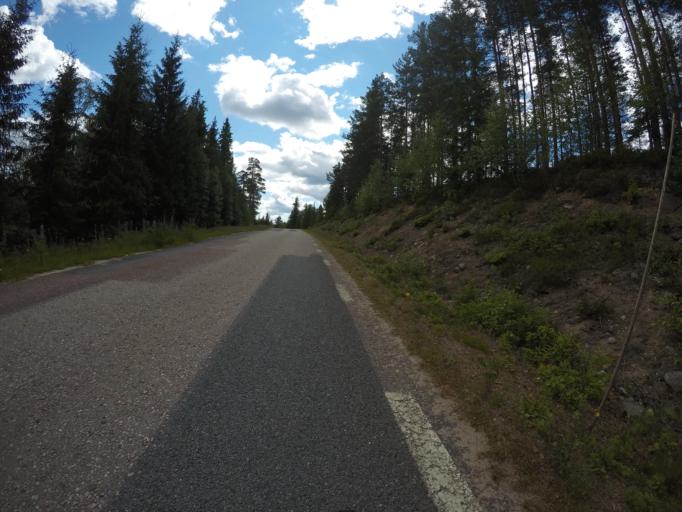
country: SE
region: OErebro
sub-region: Hallefors Kommun
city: Haellefors
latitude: 60.0636
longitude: 14.4930
